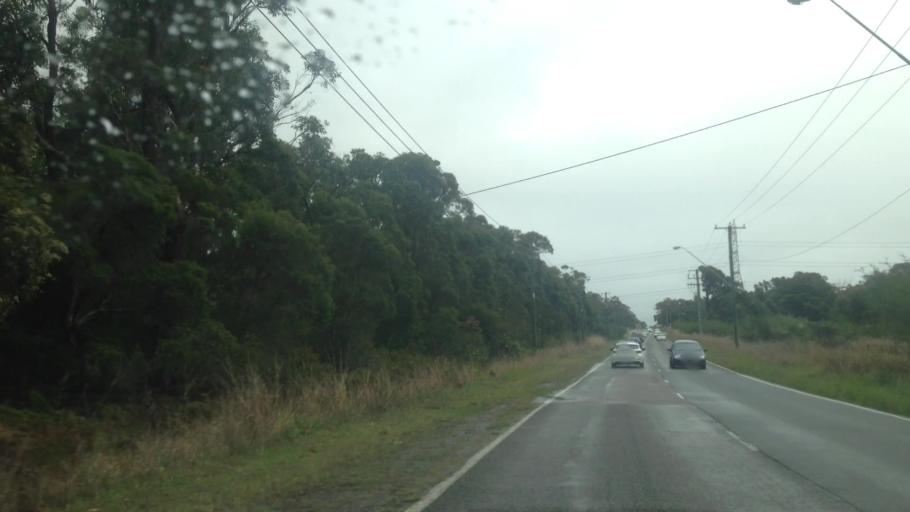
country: AU
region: New South Wales
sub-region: Wyong Shire
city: Charmhaven
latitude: -33.1610
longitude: 151.4784
